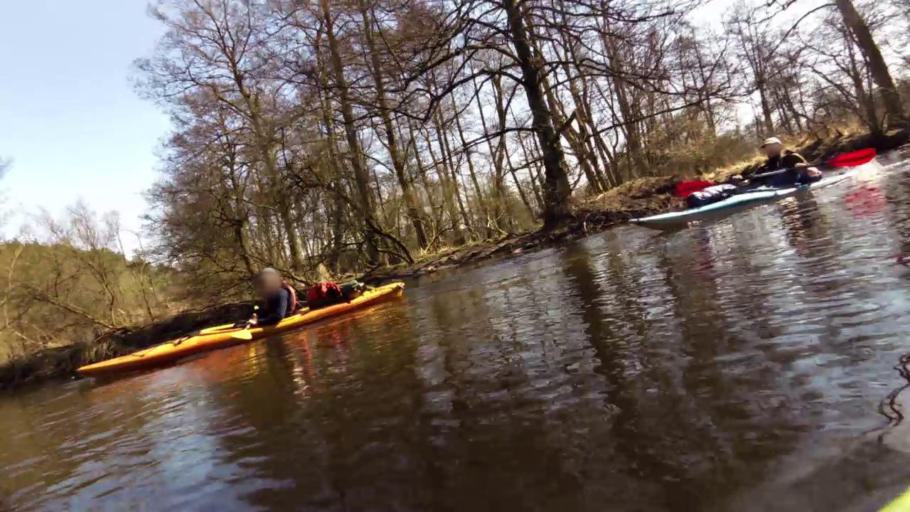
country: PL
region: West Pomeranian Voivodeship
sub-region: Powiat lobeski
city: Lobez
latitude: 53.6843
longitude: 15.5609
